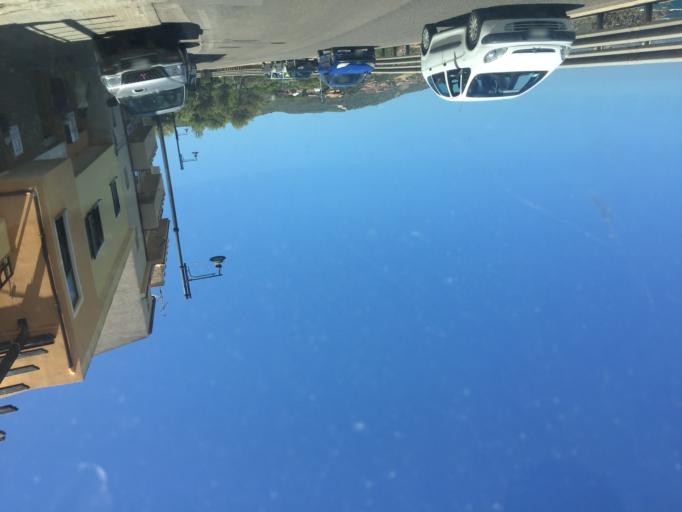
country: IT
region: Sardinia
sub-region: Provincia di Sassari
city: Castelsardo
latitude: 40.9127
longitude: 8.7158
